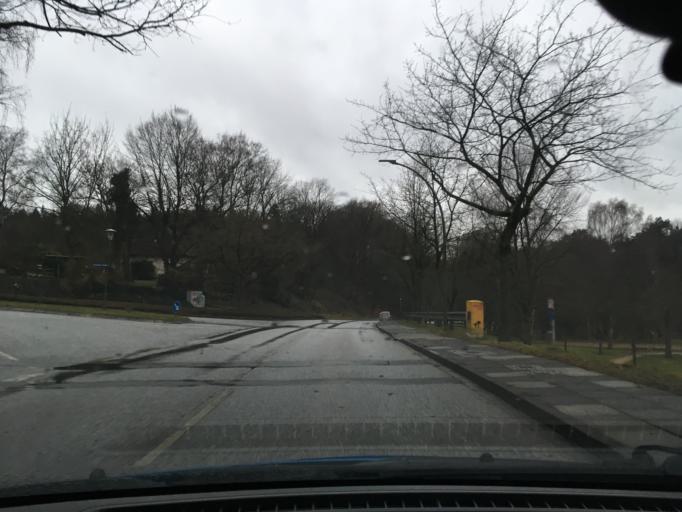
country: DE
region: Schleswig-Holstein
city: Wiershop
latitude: 53.4096
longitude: 10.4355
